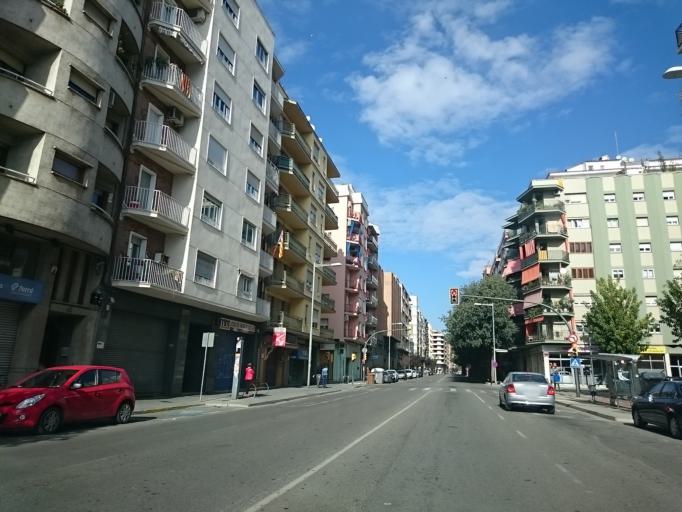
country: ES
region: Catalonia
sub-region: Provincia de Lleida
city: Lleida
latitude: 41.6100
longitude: 0.6336
